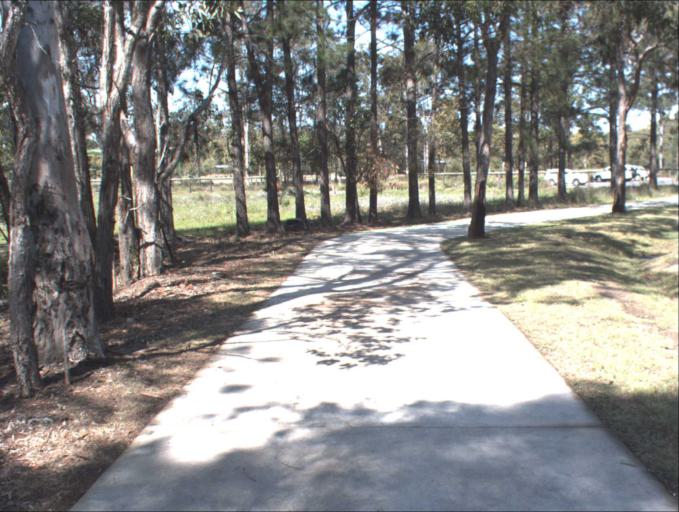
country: AU
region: Queensland
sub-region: Logan
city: Woodridge
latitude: -27.6627
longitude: 153.0875
